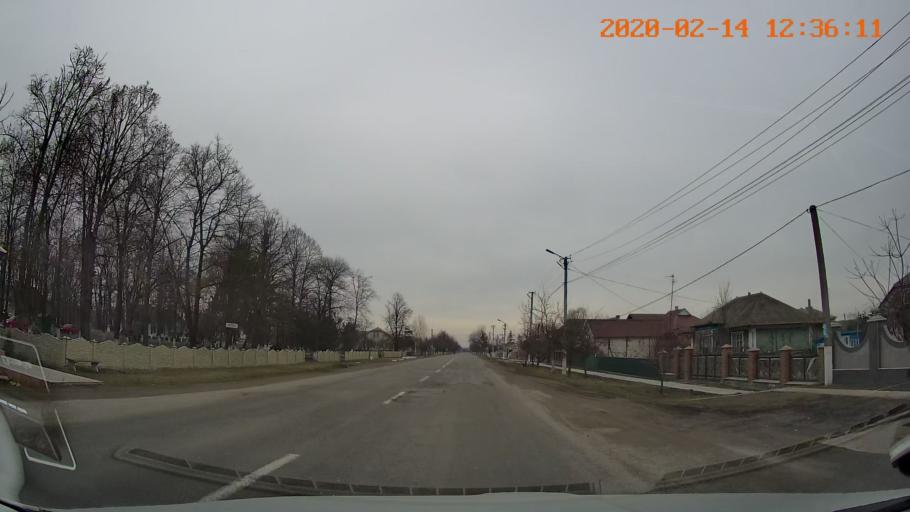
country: RO
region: Botosani
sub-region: Comuna Darabani
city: Bajura
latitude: 48.2238
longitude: 26.5026
